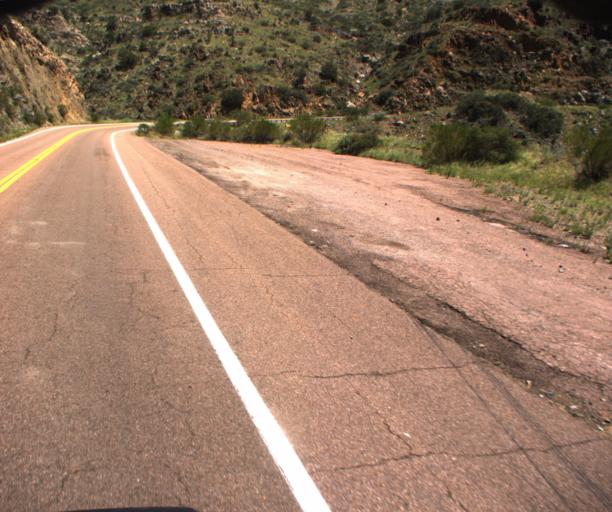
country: US
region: Arizona
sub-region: Navajo County
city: Cibecue
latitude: 33.8054
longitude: -110.4858
